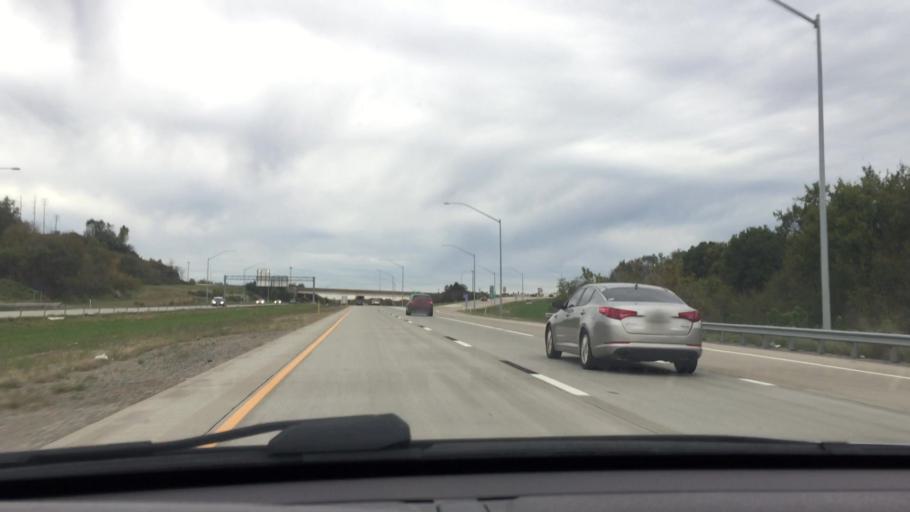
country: US
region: Pennsylvania
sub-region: Allegheny County
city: Imperial
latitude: 40.4955
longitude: -80.2774
